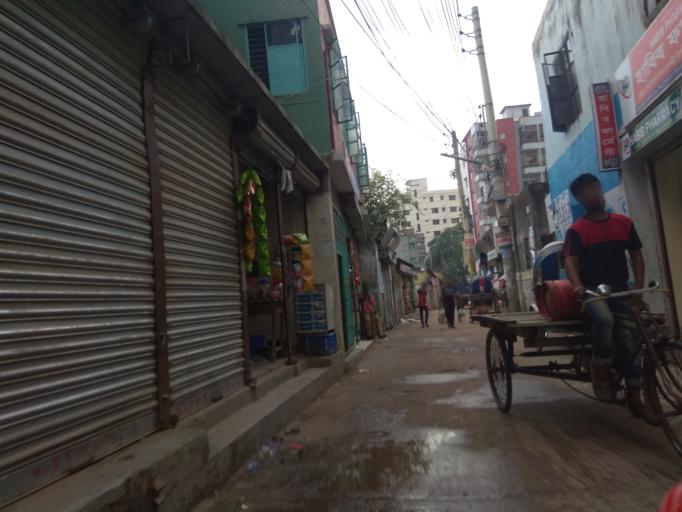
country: BD
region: Dhaka
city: Azimpur
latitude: 23.7928
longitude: 90.3673
